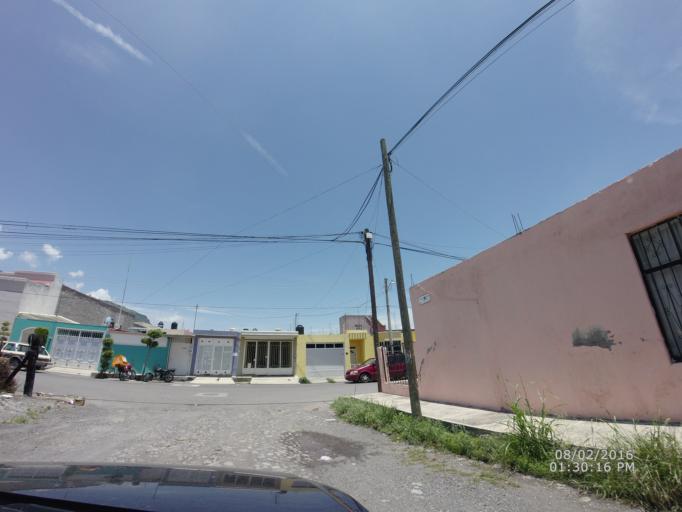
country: MX
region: Nayarit
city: Ixtlan del Rio
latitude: 21.0417
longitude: -104.3743
